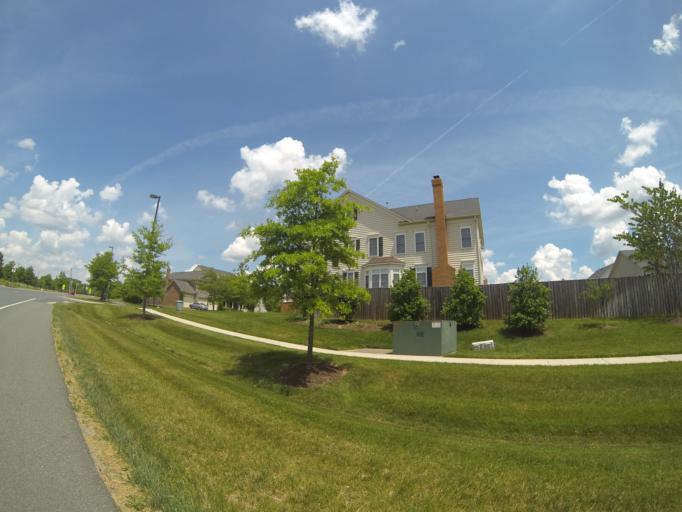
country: US
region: Maryland
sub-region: Montgomery County
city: Clarksburg
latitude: 39.2355
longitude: -77.2608
